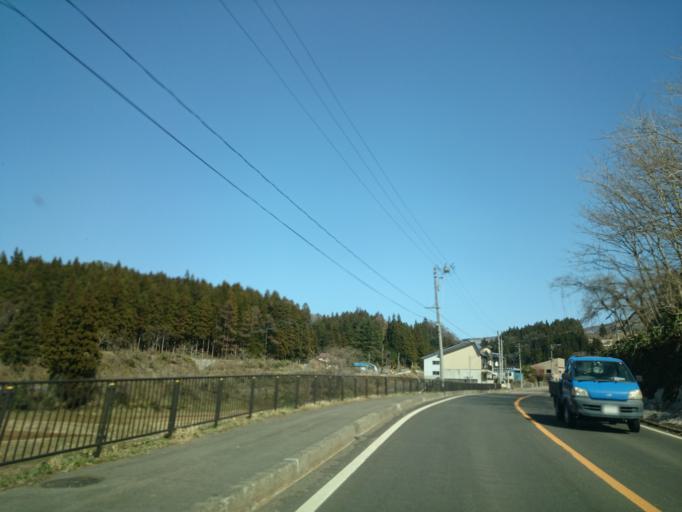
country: JP
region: Fukushima
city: Kitakata
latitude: 37.6686
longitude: 139.9758
